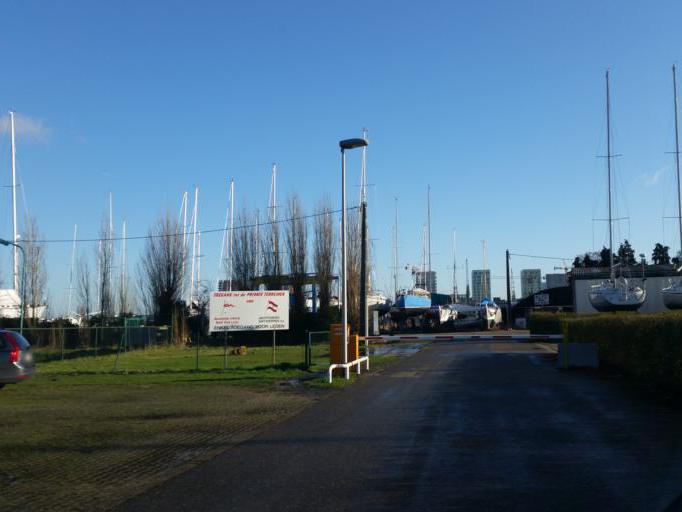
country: BE
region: Flanders
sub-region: Provincie Antwerpen
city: Antwerpen
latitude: 51.2325
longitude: 4.3936
